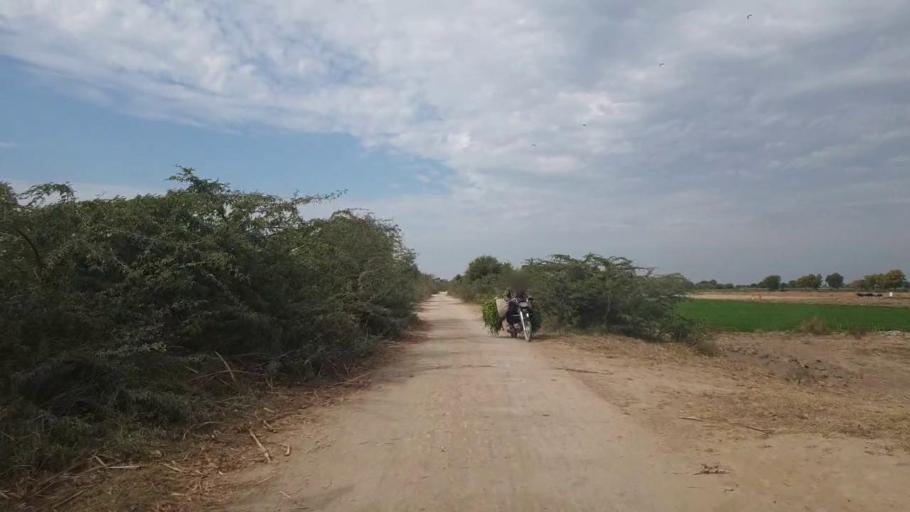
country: PK
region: Sindh
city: Jhol
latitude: 26.0102
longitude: 68.8697
